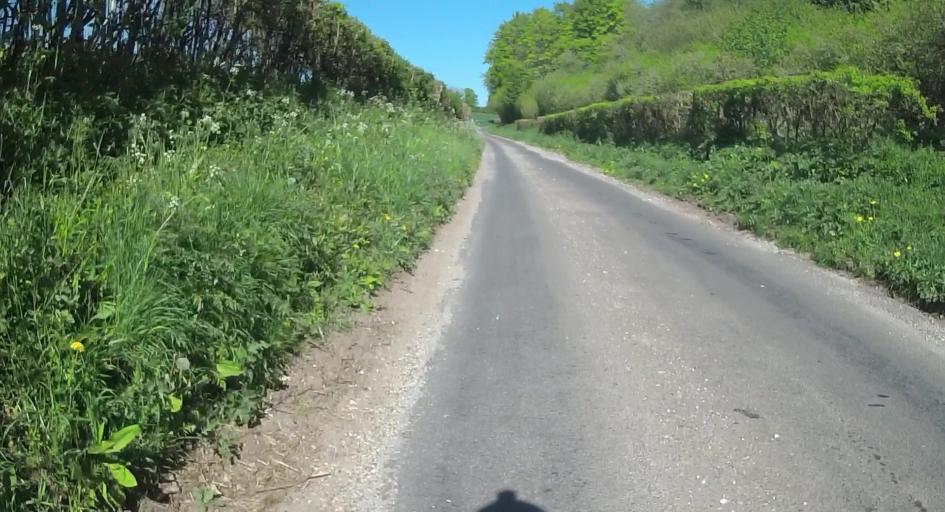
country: GB
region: England
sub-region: Hampshire
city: Alton
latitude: 51.1682
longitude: -1.0183
